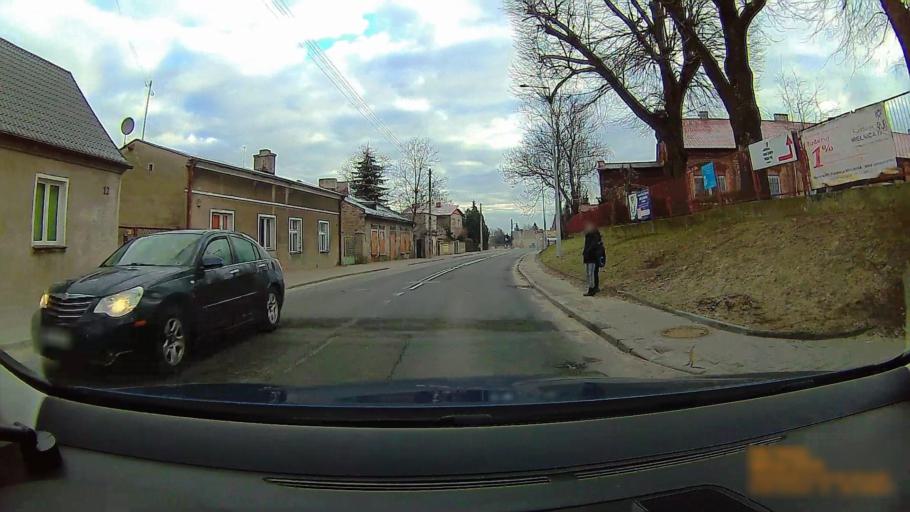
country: PL
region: Greater Poland Voivodeship
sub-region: Konin
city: Konin
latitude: 52.2045
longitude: 18.2450
